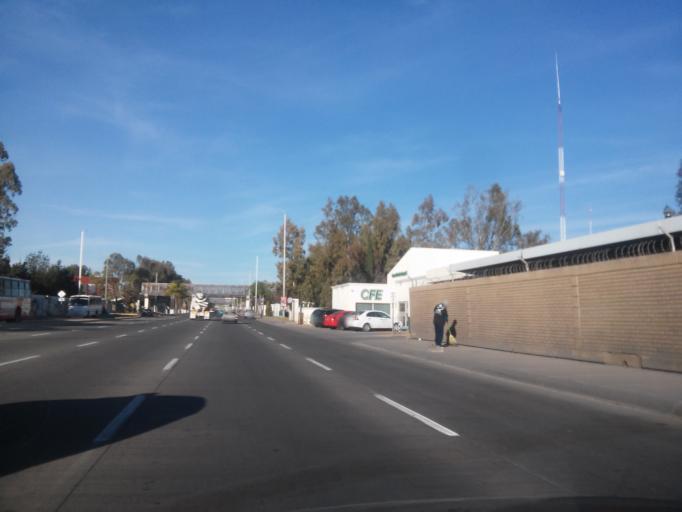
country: MX
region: Durango
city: Victoria de Durango
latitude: 24.0338
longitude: -104.6432
